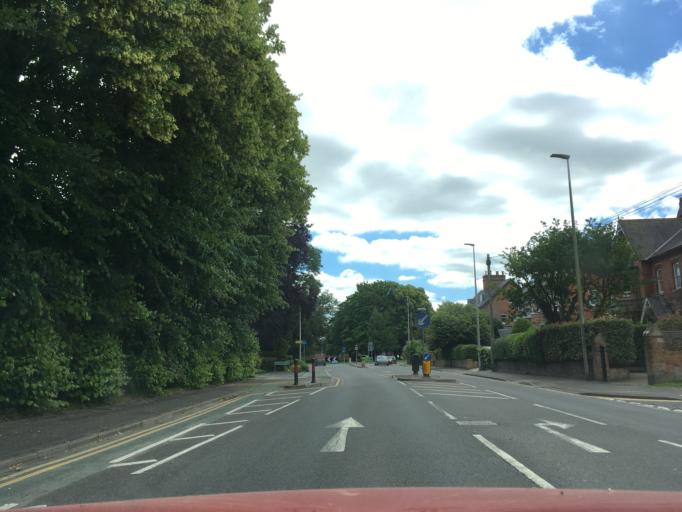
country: GB
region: England
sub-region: West Berkshire
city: Newbury
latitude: 51.4088
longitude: -1.3298
